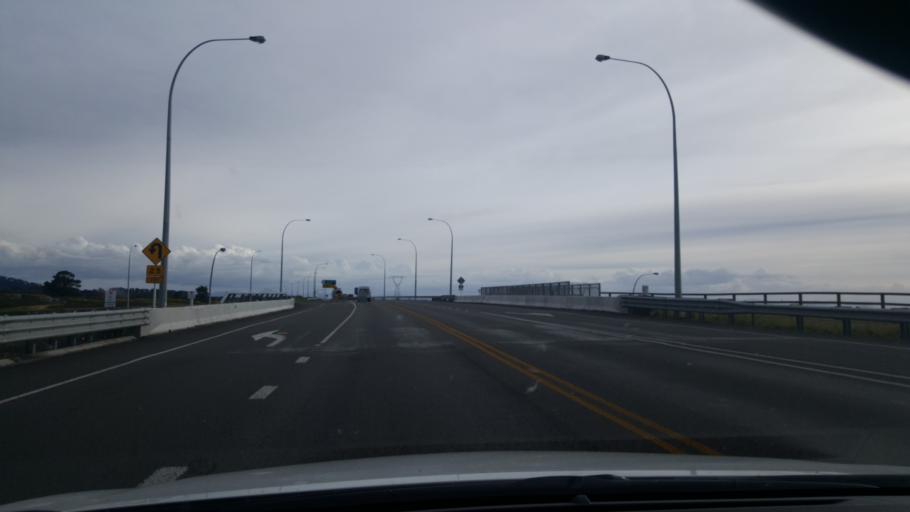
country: NZ
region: Waikato
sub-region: Taupo District
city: Taupo
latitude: -38.6821
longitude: 176.1152
